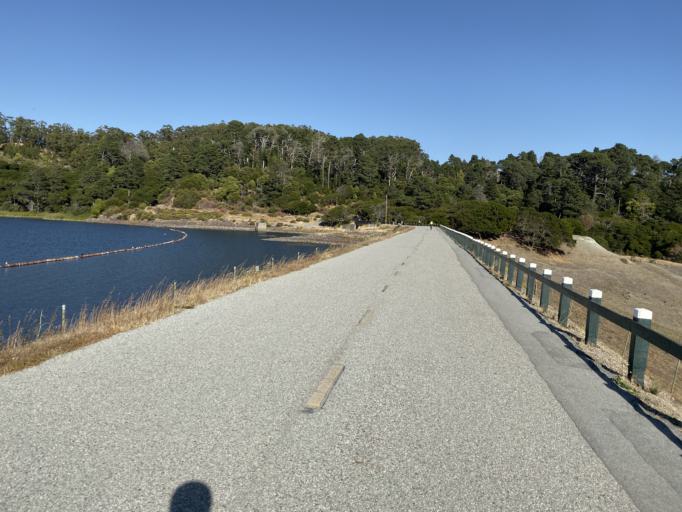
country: US
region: California
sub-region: San Mateo County
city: Millbrae
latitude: 37.5799
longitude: -122.4123
